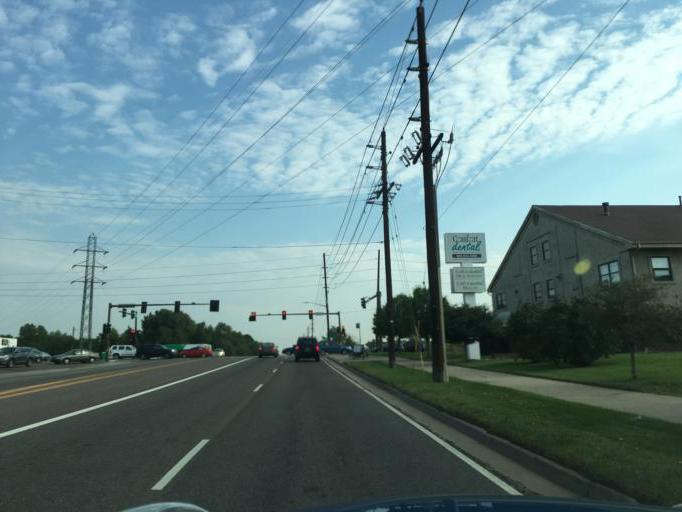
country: US
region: Colorado
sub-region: Jefferson County
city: Wheat Ridge
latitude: 39.7539
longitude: -105.1095
